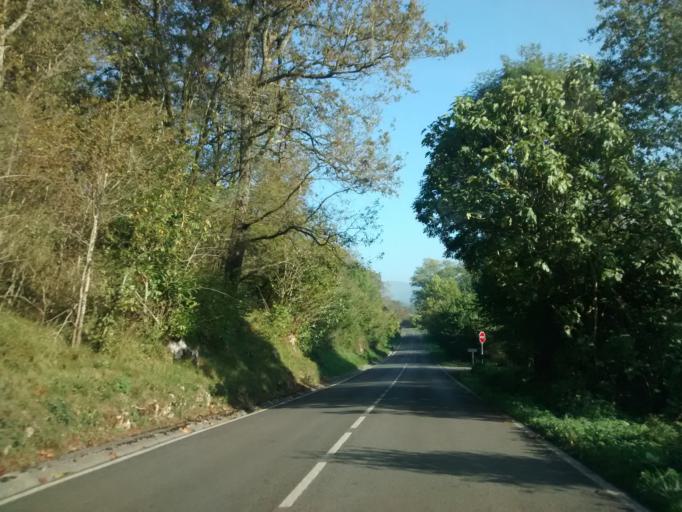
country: ES
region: Cantabria
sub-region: Provincia de Cantabria
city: Entrambasaguas
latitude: 43.3458
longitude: -3.6892
